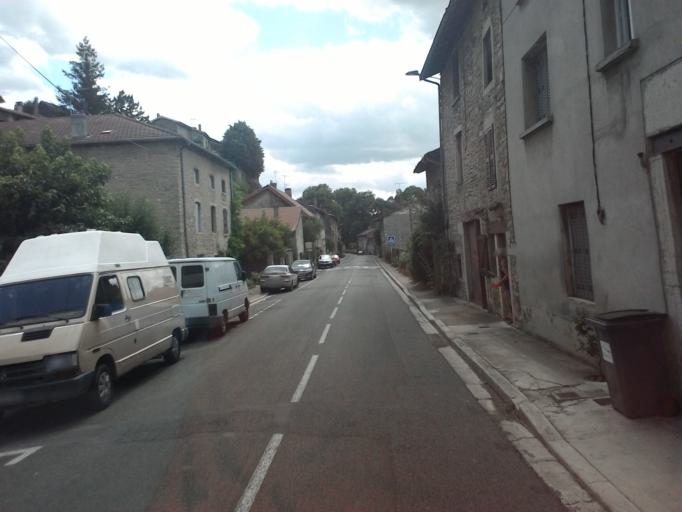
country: FR
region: Rhone-Alpes
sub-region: Departement de l'Ain
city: Saint-Sorlin-en-Bugey
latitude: 45.8834
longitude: 5.3723
